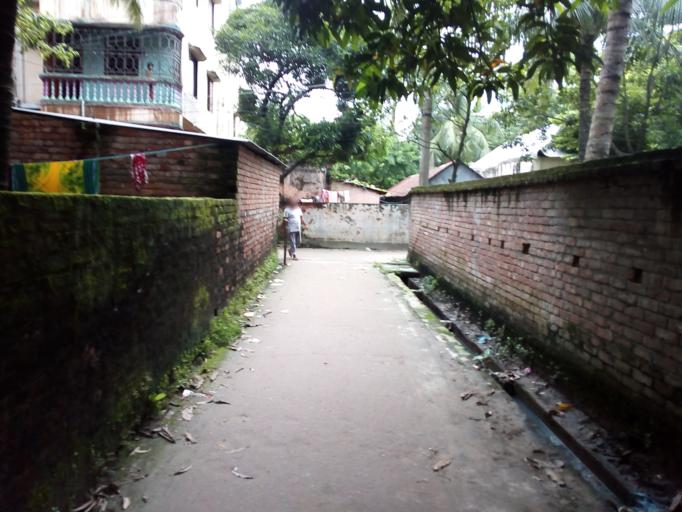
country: BD
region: Dhaka
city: Tungi
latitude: 23.8435
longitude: 90.2504
